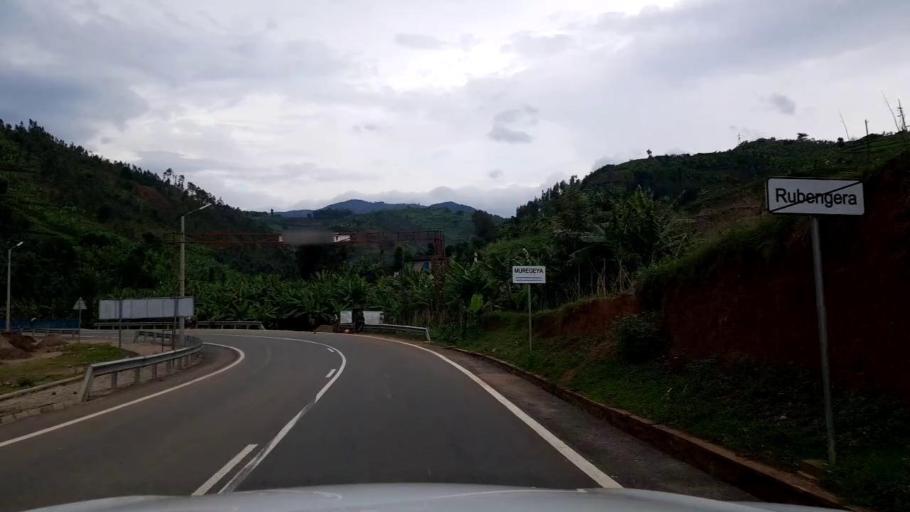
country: RW
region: Western Province
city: Kibuye
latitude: -2.0316
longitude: 29.3991
